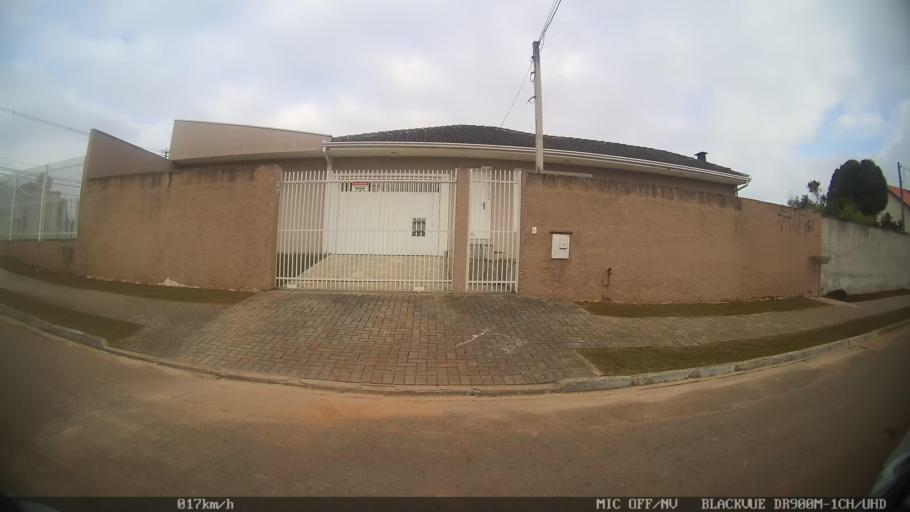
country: BR
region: Parana
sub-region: Curitiba
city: Curitiba
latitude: -25.3979
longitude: -49.3188
